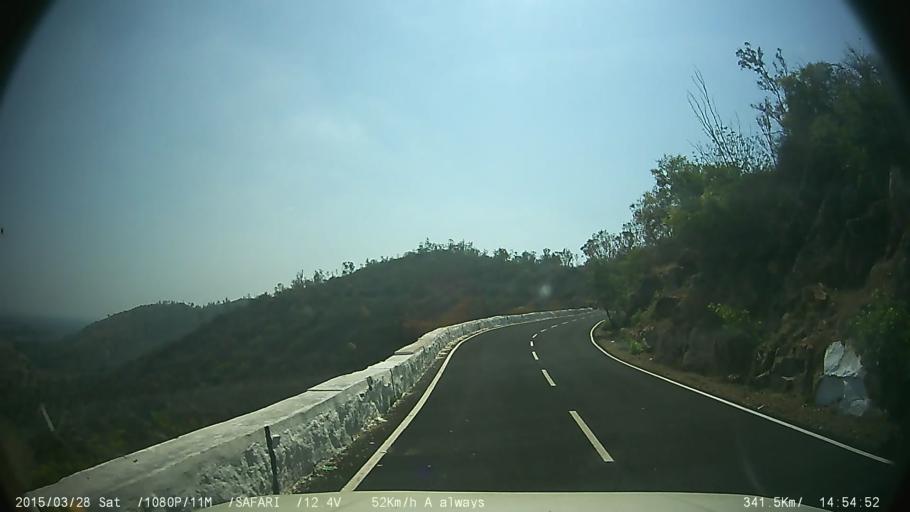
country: IN
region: Karnataka
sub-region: Mysore
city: Mysore
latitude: 12.2821
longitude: 76.6917
